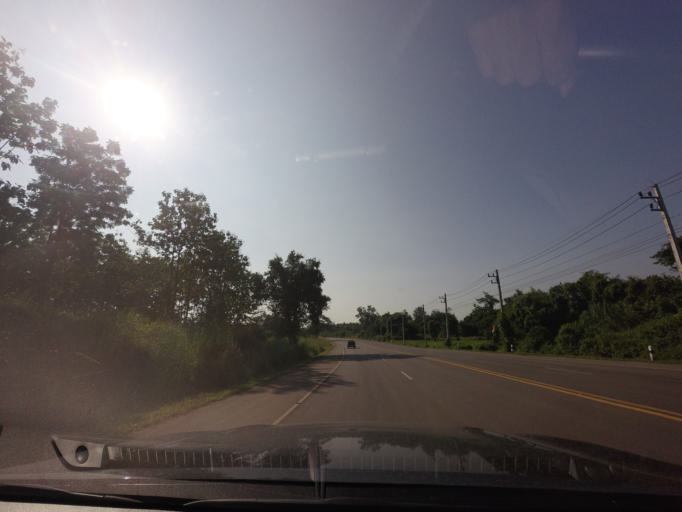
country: TH
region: Phetchabun
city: Lom Kao
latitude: 16.8425
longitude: 101.1780
